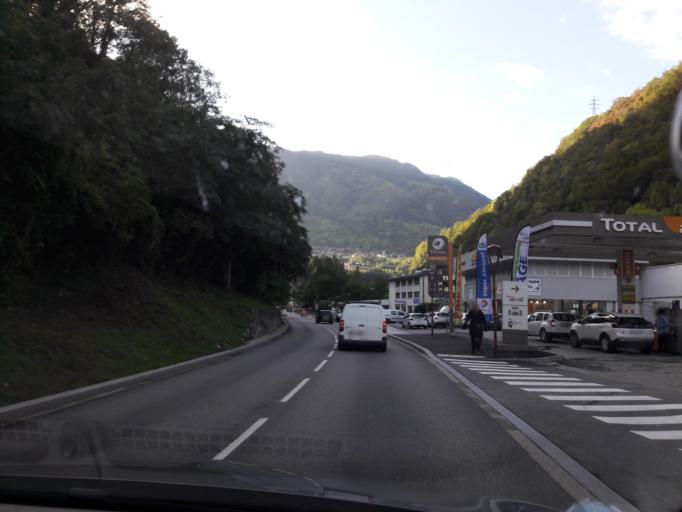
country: FR
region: Rhone-Alpes
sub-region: Departement de la Savoie
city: Salins-les-Thermes
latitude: 45.4769
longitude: 6.5275
